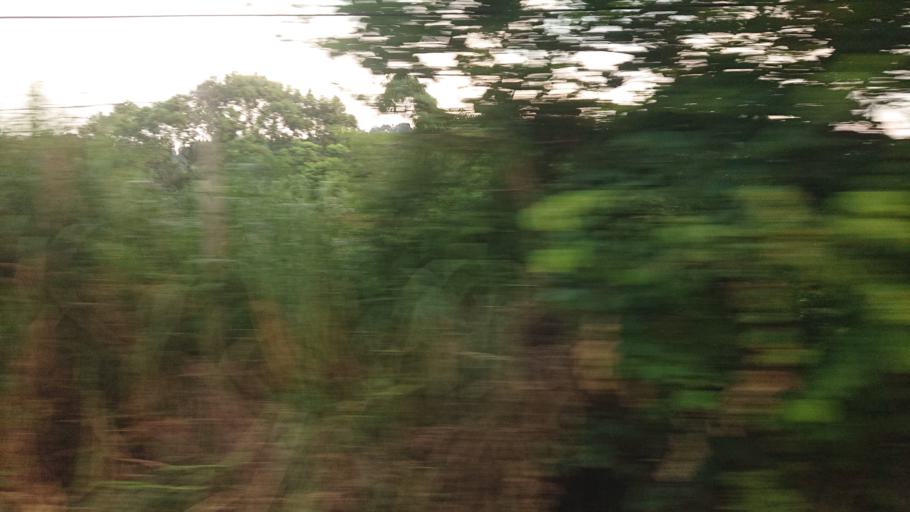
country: TW
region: Taiwan
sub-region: Nantou
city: Puli
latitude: 23.9739
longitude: 120.9920
